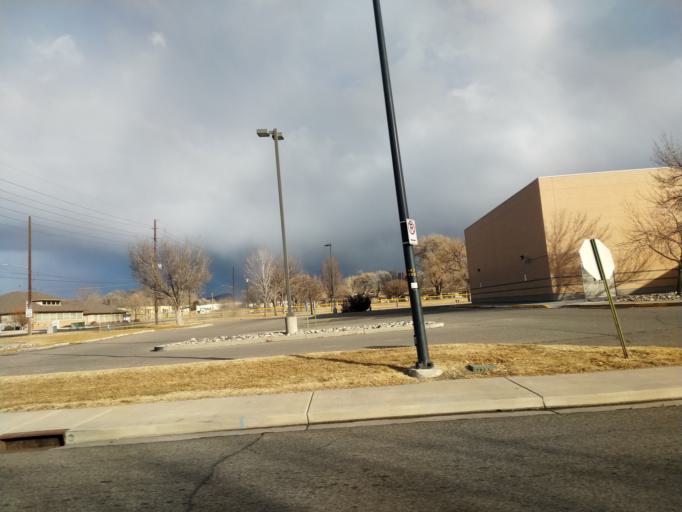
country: US
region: Colorado
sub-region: Mesa County
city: Grand Junction
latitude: 39.0913
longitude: -108.5801
